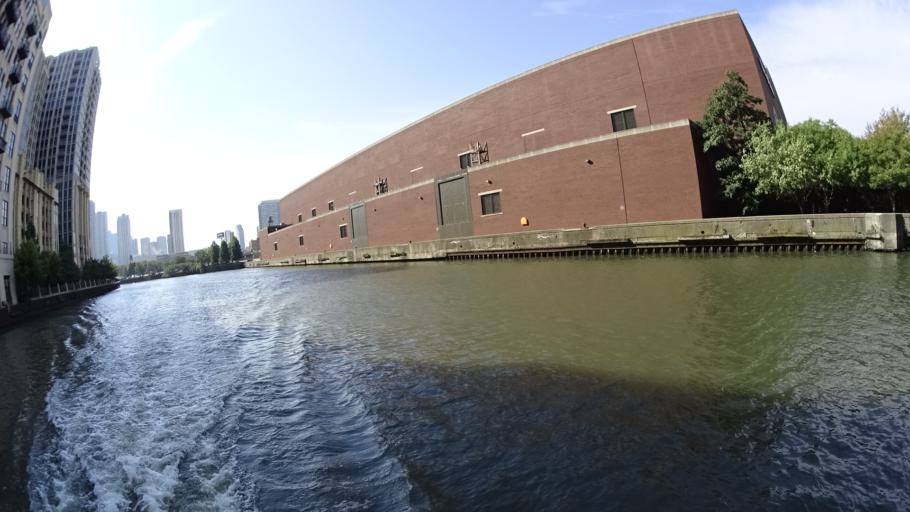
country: US
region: Illinois
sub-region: Cook County
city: Chicago
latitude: 41.8959
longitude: -87.6440
